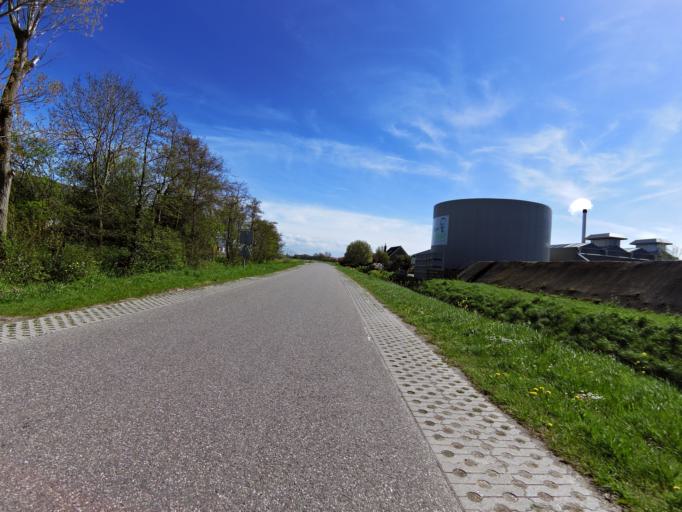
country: NL
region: South Holland
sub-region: Gemeente Brielle
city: Brielle
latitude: 51.9043
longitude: 4.1327
